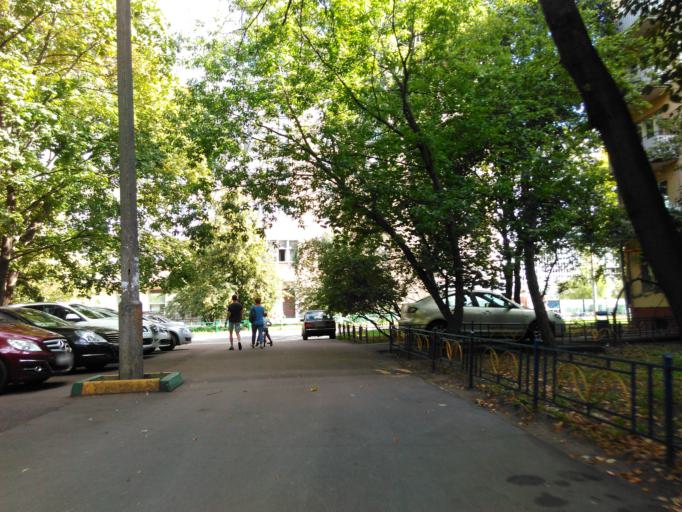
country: RU
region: Moscow
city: Nikol'skoye
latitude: 55.6765
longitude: 37.5028
